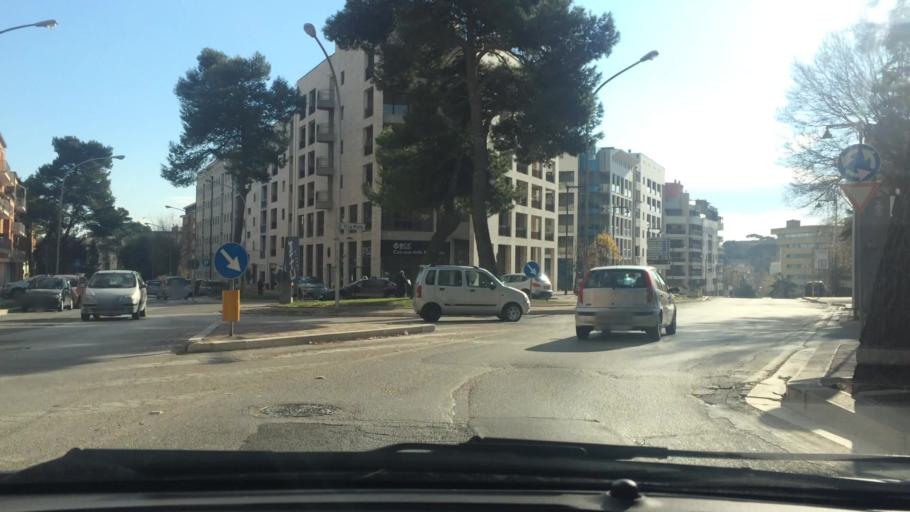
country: IT
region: Basilicate
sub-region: Provincia di Matera
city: Matera
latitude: 40.6693
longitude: 16.5990
